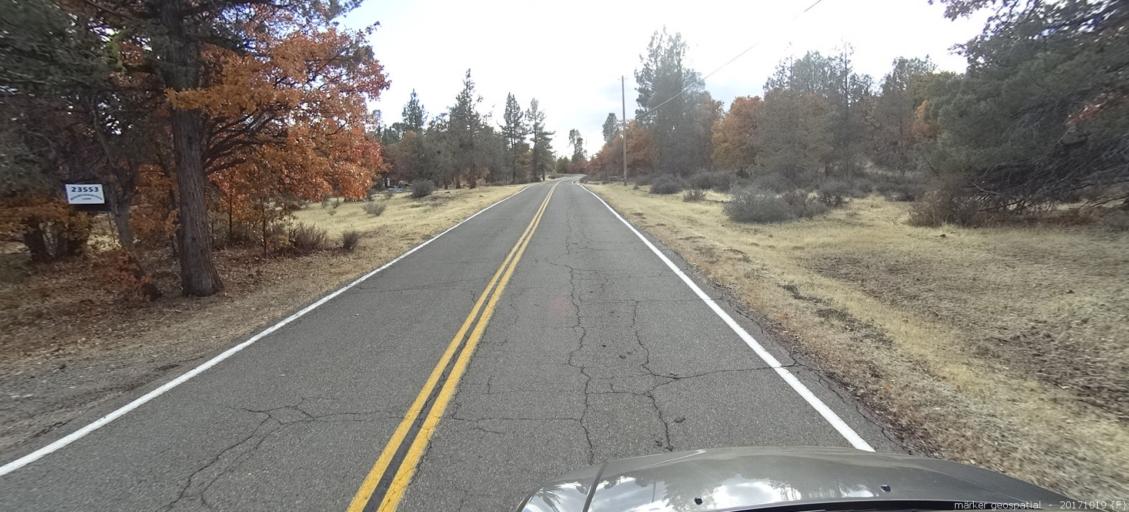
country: US
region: California
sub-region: Shasta County
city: Burney
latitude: 40.9686
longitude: -121.4339
